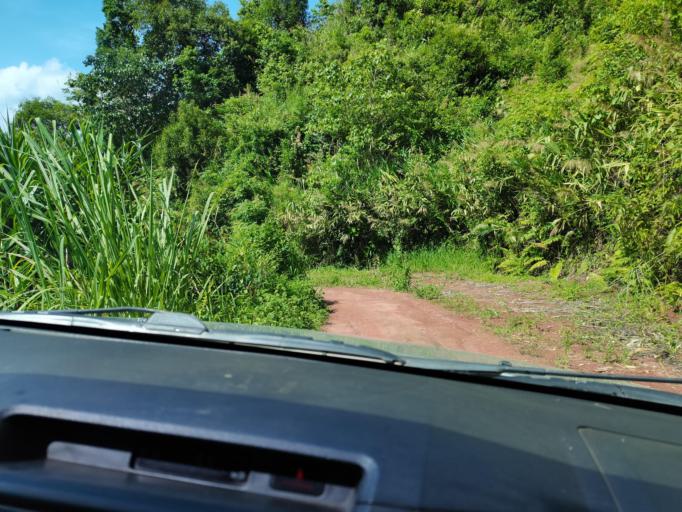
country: LA
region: Loungnamtha
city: Muang Nale
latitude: 20.5585
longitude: 101.0582
